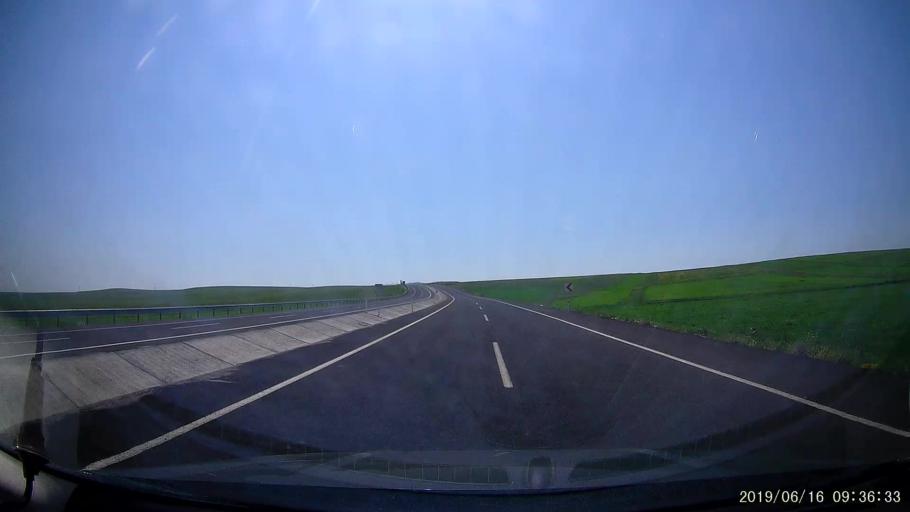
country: TR
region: Kars
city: Kars
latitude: 40.5570
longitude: 43.1749
